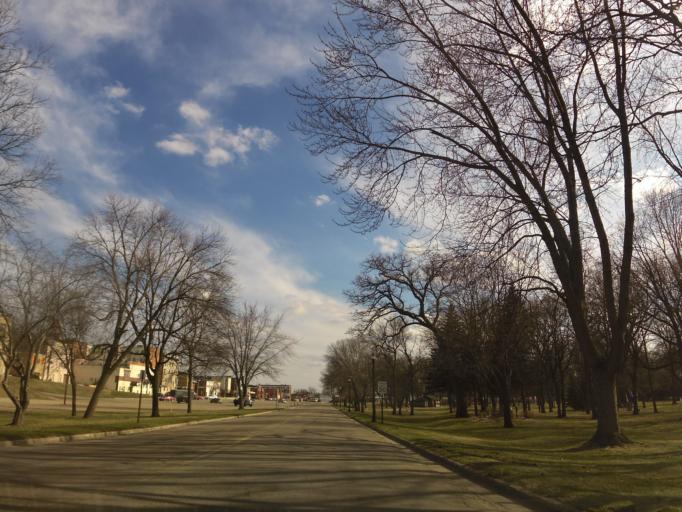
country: US
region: Minnesota
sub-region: Chippewa County
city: Montevideo
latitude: 44.9480
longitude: -95.7269
